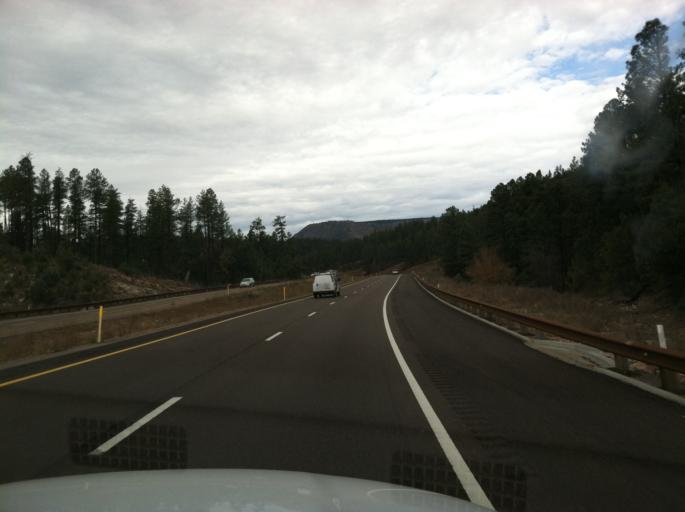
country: US
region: Arizona
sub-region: Gila County
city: Star Valley
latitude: 34.3253
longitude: -111.0854
